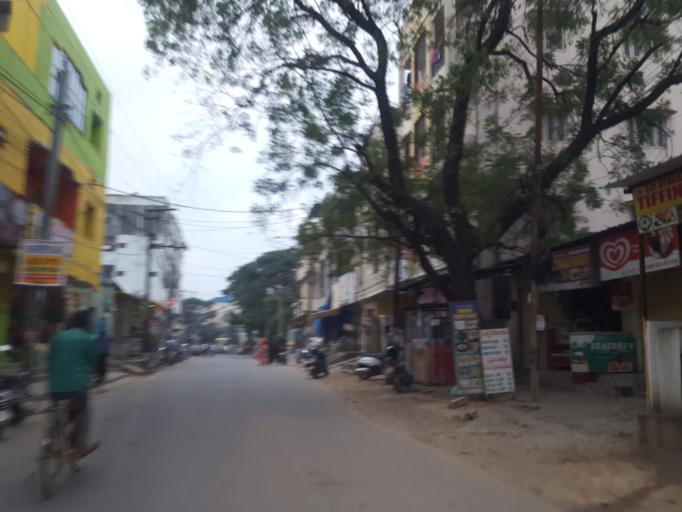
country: IN
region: Telangana
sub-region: Medak
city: Serilingampalle
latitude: 17.4932
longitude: 78.3318
